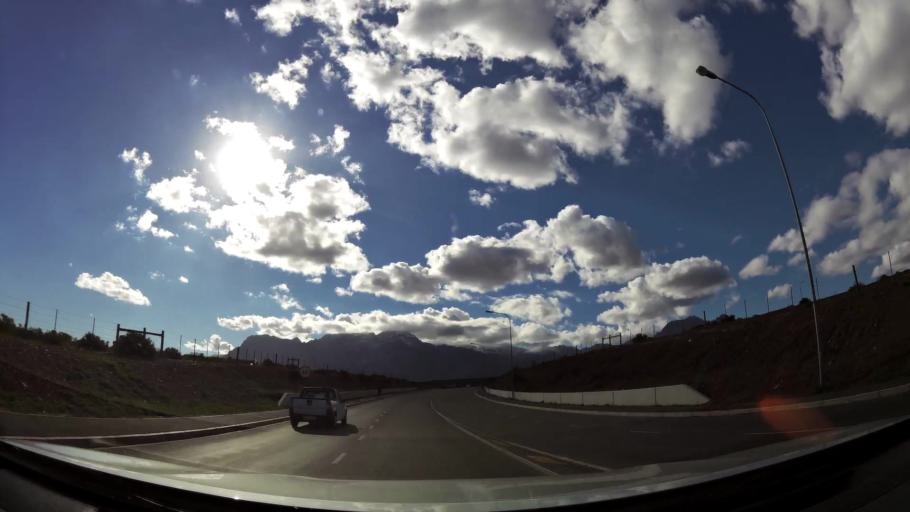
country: ZA
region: Western Cape
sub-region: Cape Winelands District Municipality
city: Worcester
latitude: -33.6343
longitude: 19.4275
